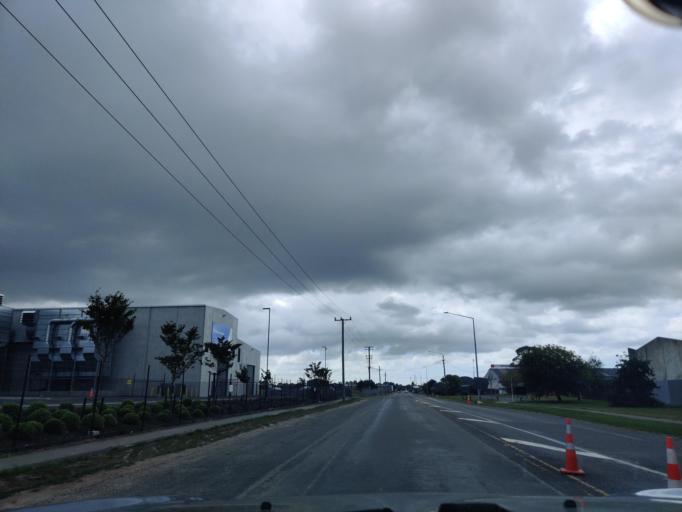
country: NZ
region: Canterbury
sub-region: Selwyn District
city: Prebbleton
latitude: -43.5547
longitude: 172.5129
